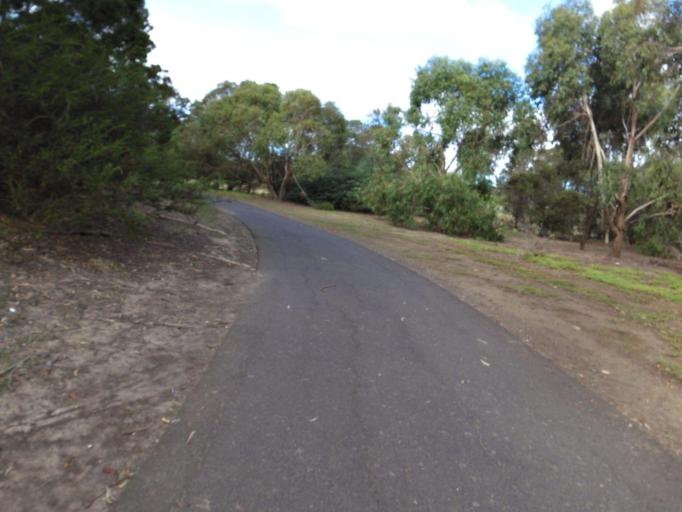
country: AU
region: Victoria
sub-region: Greater Geelong
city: Wandana Heights
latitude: -38.2055
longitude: 144.3075
